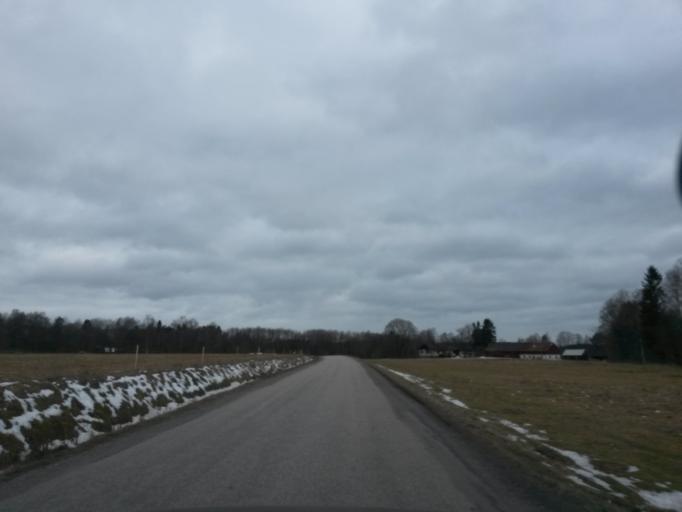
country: SE
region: Vaestra Goetaland
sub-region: Vargarda Kommun
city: Vargarda
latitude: 58.0327
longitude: 12.8722
